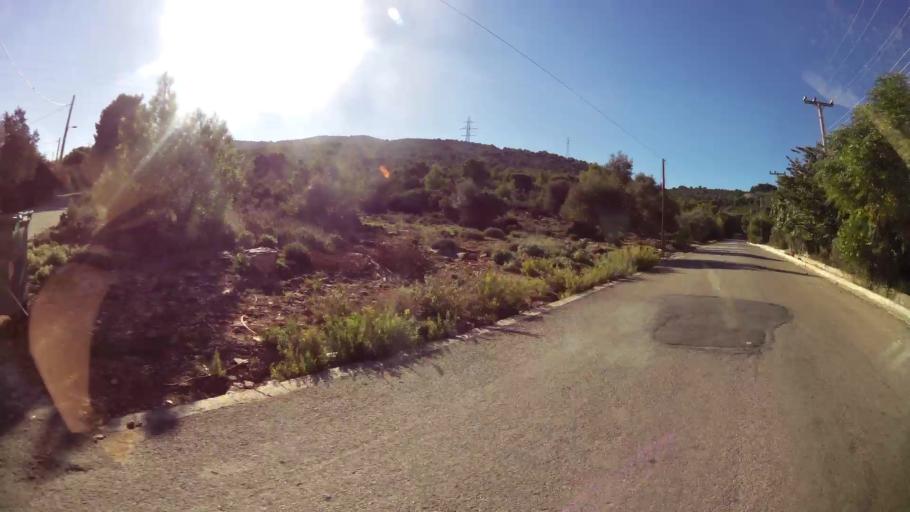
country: GR
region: Attica
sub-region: Nomarchia Anatolikis Attikis
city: Leondarion
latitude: 37.9947
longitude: 23.8413
